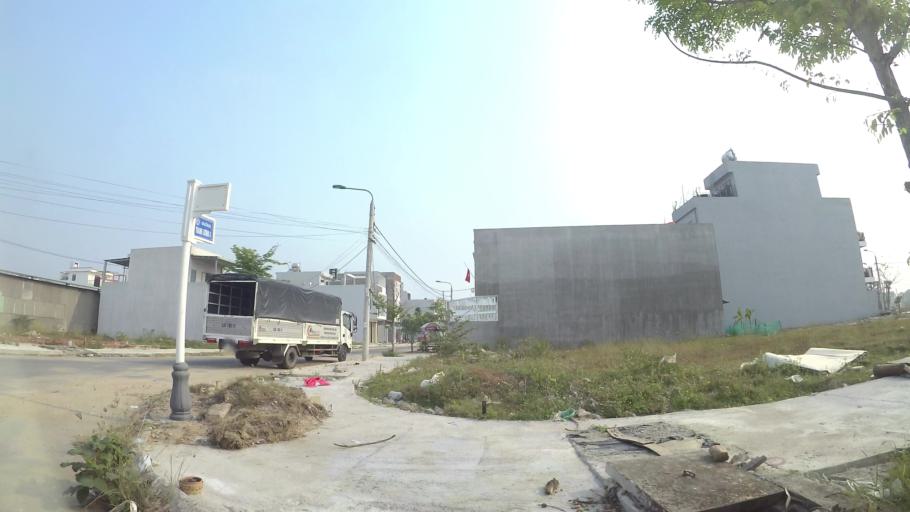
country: VN
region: Da Nang
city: Ngu Hanh Son
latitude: 16.0056
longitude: 108.2282
